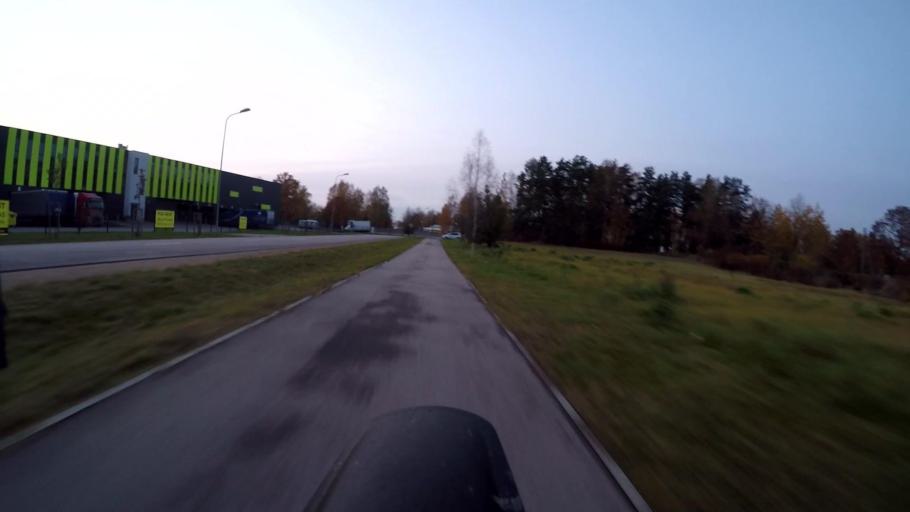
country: LV
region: Marupe
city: Marupe
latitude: 56.9179
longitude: 23.9901
